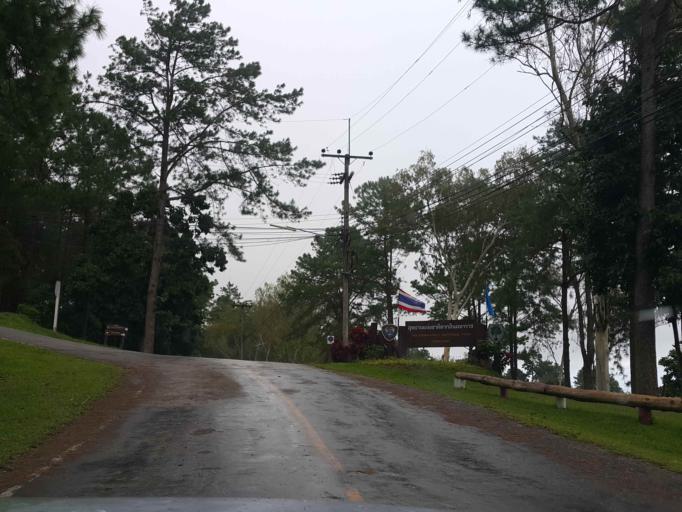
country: TH
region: Tak
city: Tak
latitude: 16.7783
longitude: 98.9285
